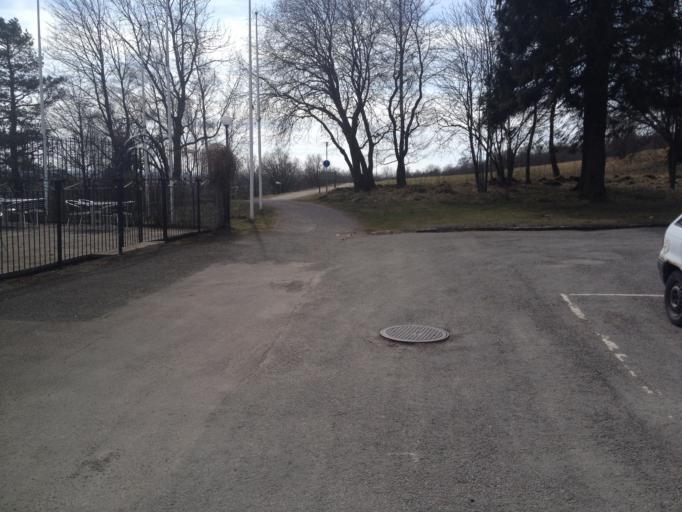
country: SE
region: Vaestra Goetaland
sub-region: Falkopings Kommun
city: Falkoeping
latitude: 58.1831
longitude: 13.5400
